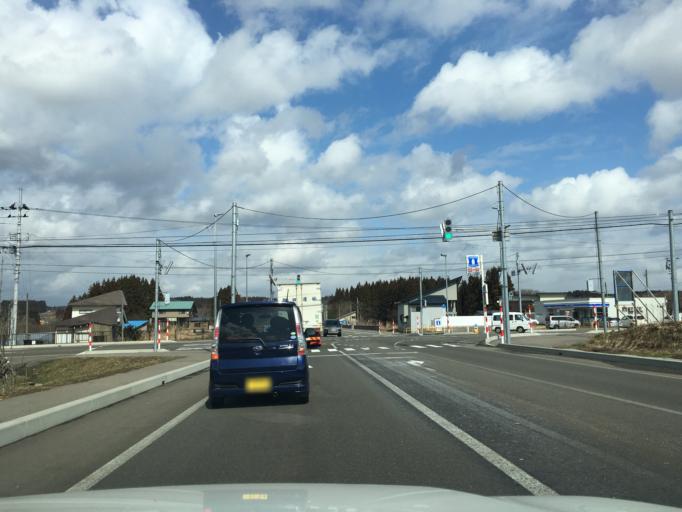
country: JP
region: Akita
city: Takanosu
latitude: 40.1193
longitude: 140.3786
